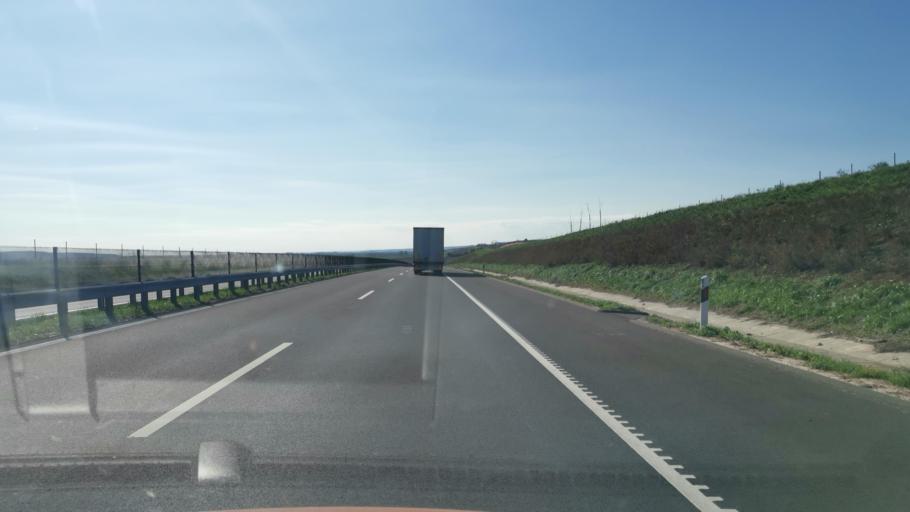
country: HU
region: Borsod-Abauj-Zemplen
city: Halmaj
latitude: 48.2776
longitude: 21.0055
